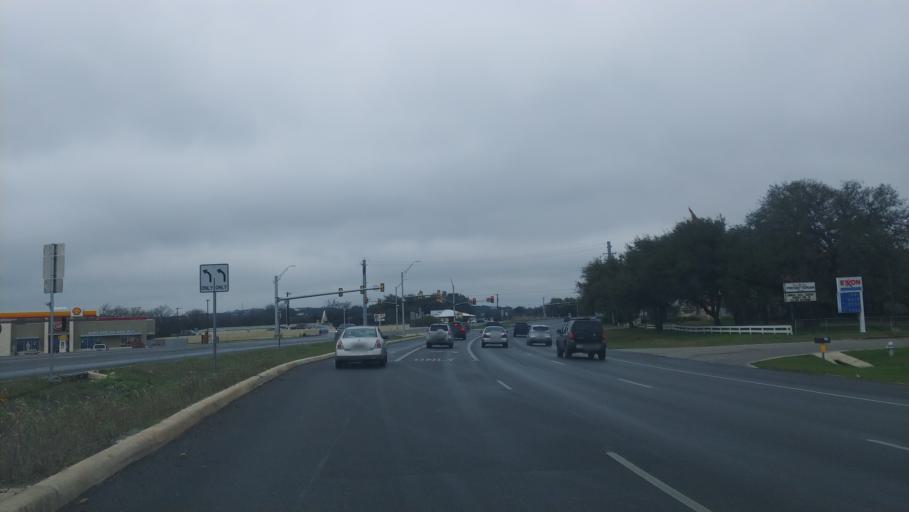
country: US
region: Texas
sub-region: Bexar County
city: Helotes
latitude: 29.5643
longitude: -98.6874
